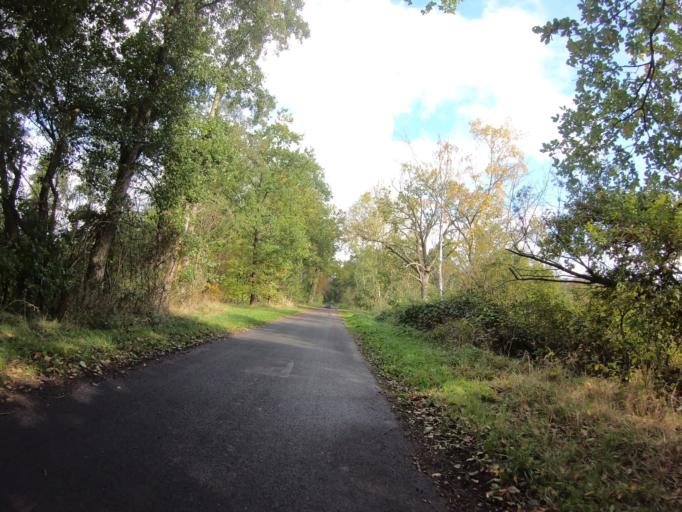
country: DE
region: Lower Saxony
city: Wagenhoff
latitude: 52.5435
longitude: 10.5502
